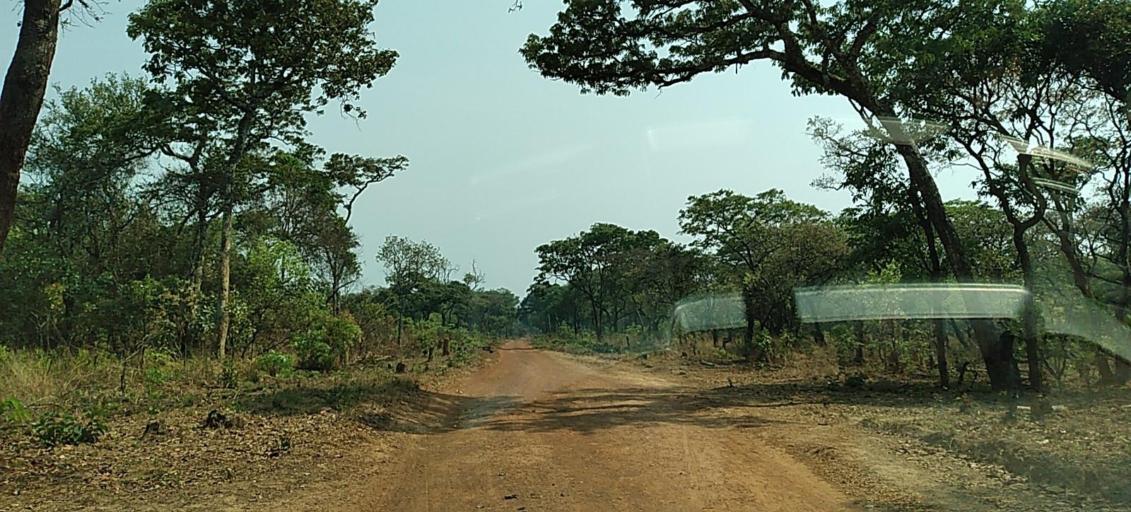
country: ZM
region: North-Western
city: Kansanshi
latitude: -12.0694
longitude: 26.8884
